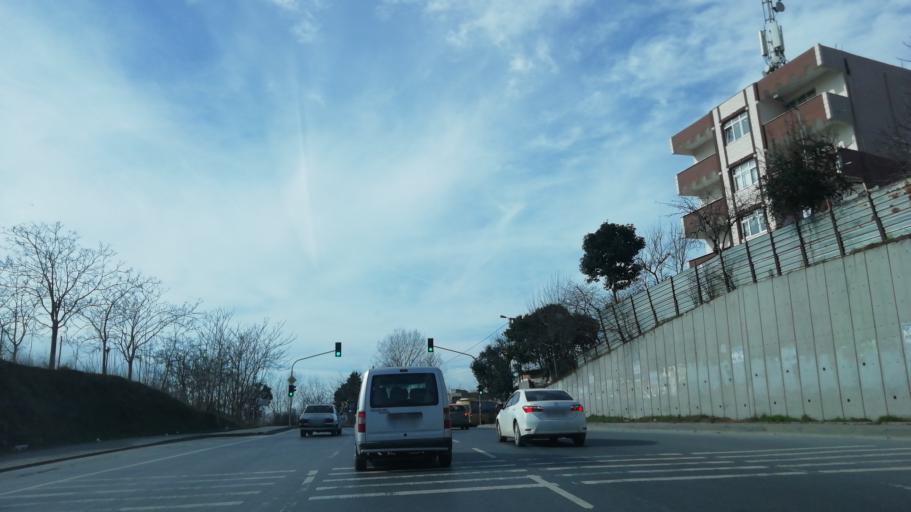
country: TR
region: Istanbul
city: Basaksehir
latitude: 41.0620
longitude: 28.7536
